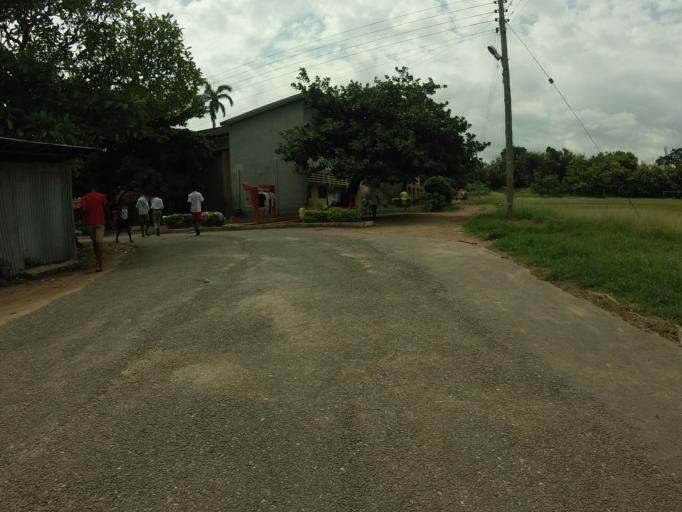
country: GH
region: Volta
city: Ho
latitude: 6.5978
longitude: 0.4750
